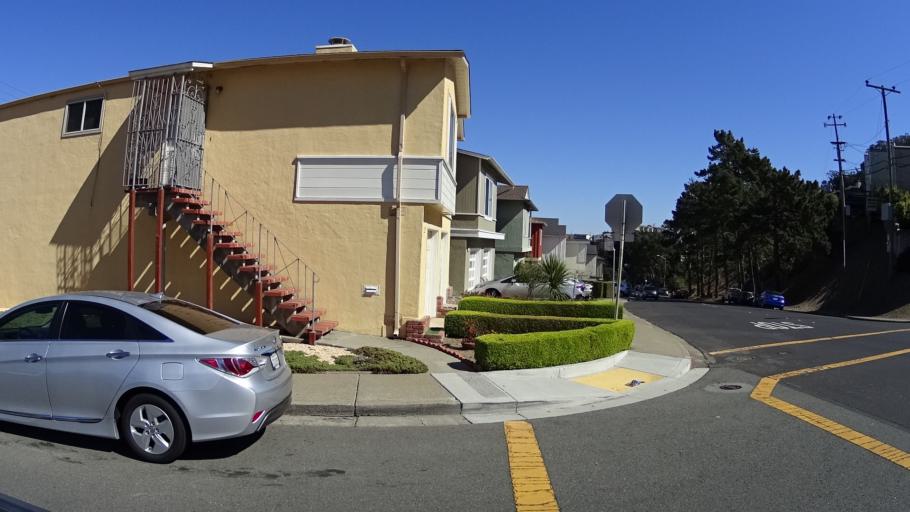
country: US
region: California
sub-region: San Mateo County
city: Daly City
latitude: 37.7064
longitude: -122.4369
